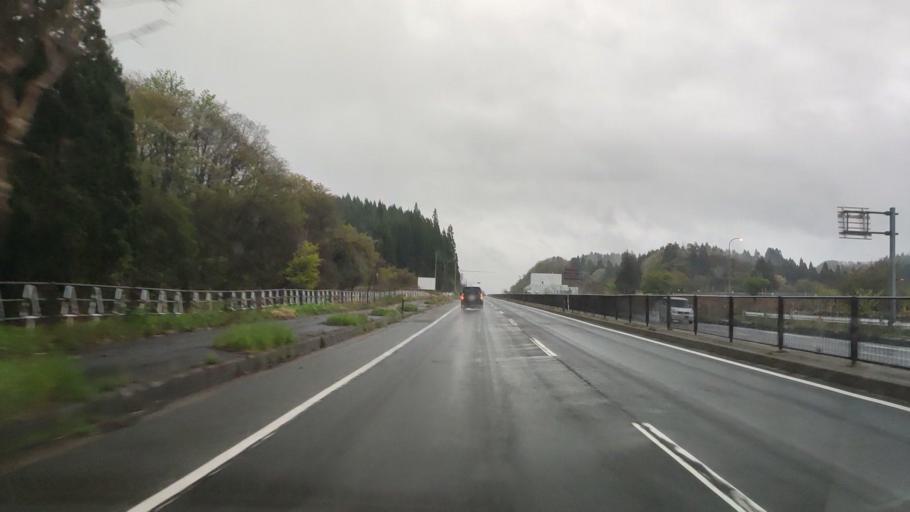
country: JP
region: Akita
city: Akita
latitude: 39.6612
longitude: 140.1910
